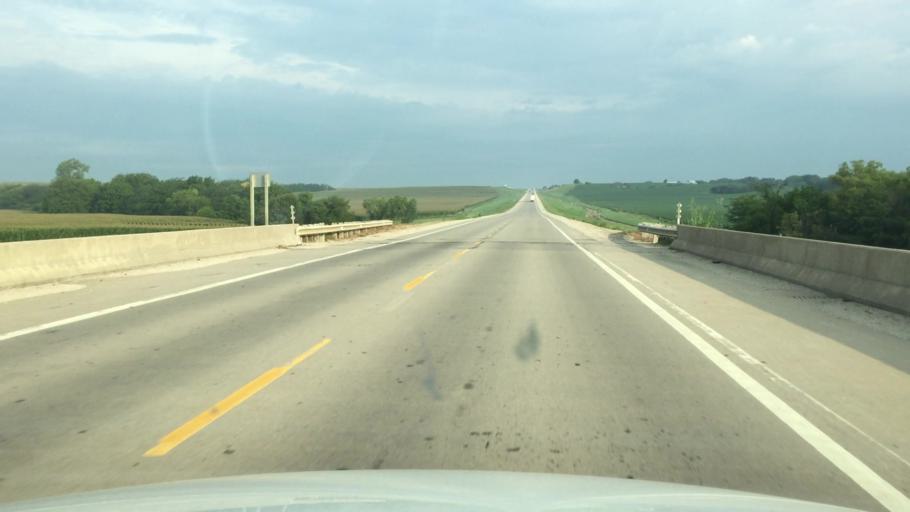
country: US
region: Kansas
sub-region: Doniphan County
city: Highland
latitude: 39.8159
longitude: -95.2030
